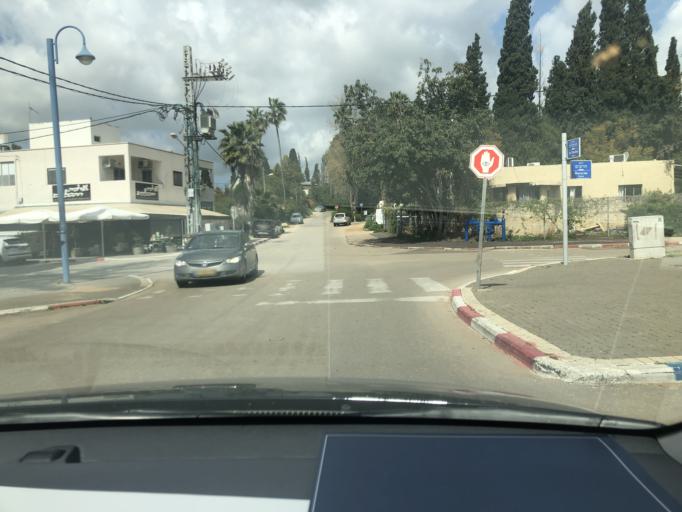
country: IL
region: Haifa
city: Hadera
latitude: 32.4767
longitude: 34.9717
